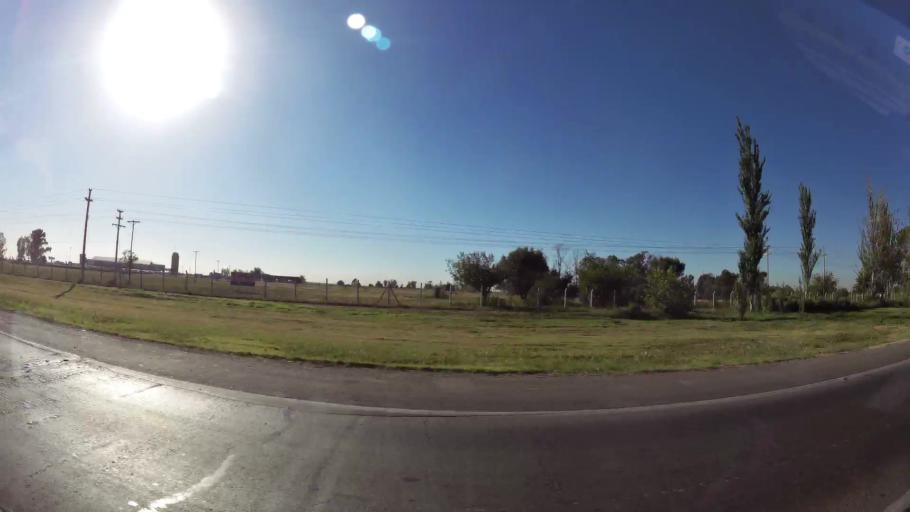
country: AR
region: Mendoza
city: Las Heras
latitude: -32.8295
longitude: -68.8056
